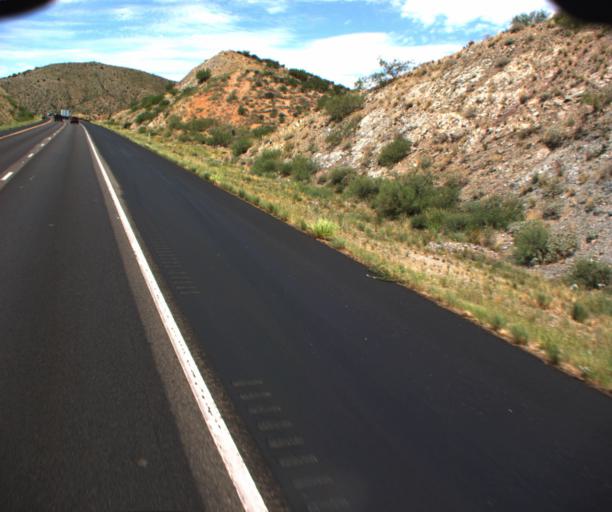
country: US
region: Arizona
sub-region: Pinal County
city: Gold Camp
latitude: 33.2746
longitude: -111.2218
